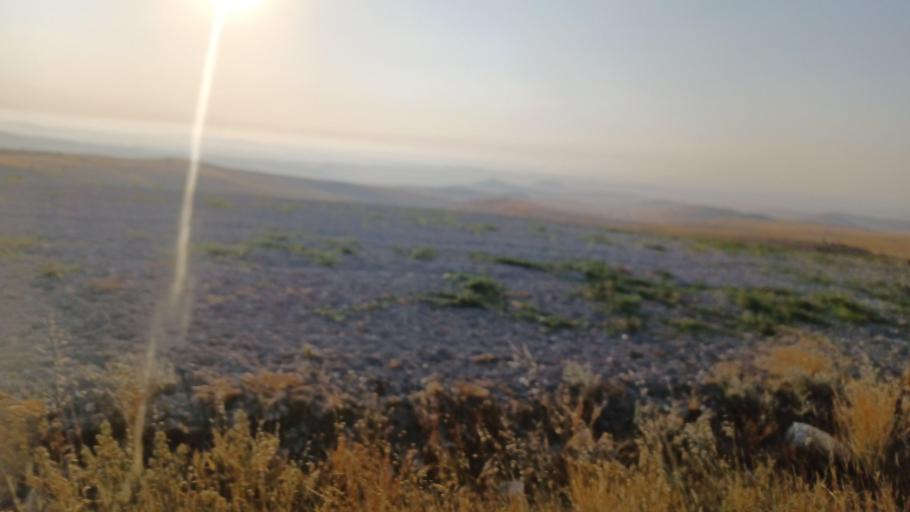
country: CY
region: Larnaka
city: Psevdas
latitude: 34.9139
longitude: 33.4857
